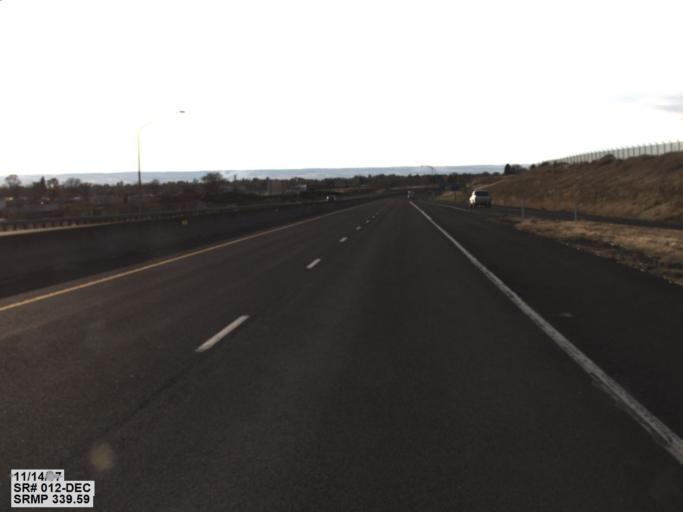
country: US
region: Washington
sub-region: Walla Walla County
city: Walla Walla East
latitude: 46.0836
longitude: -118.2868
